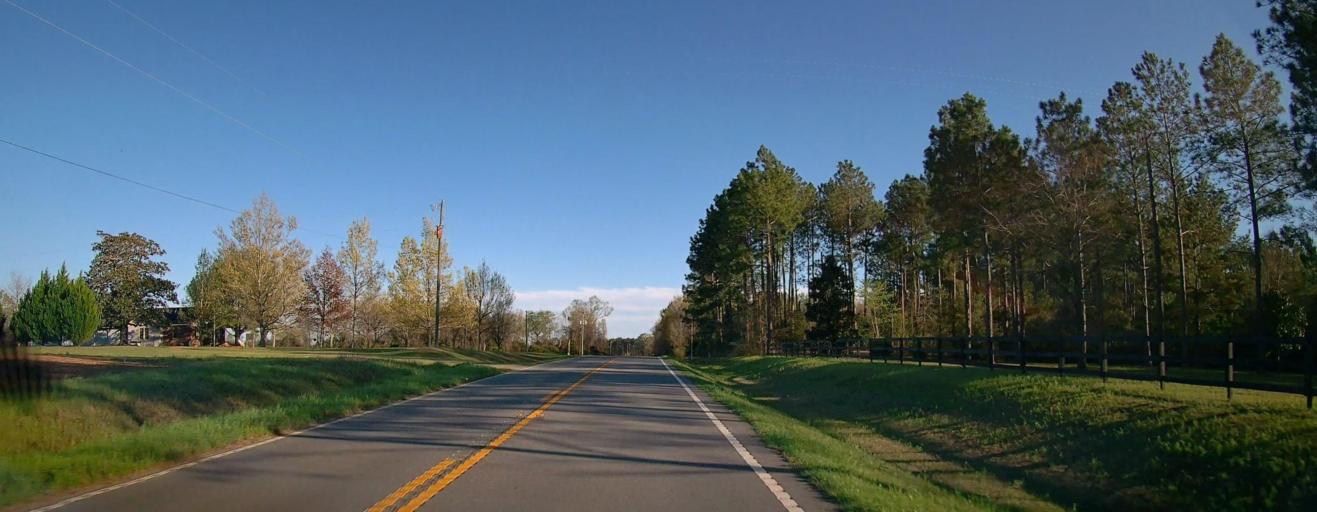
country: US
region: Georgia
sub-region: Pulaski County
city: Hawkinsville
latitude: 32.2229
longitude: -83.3897
